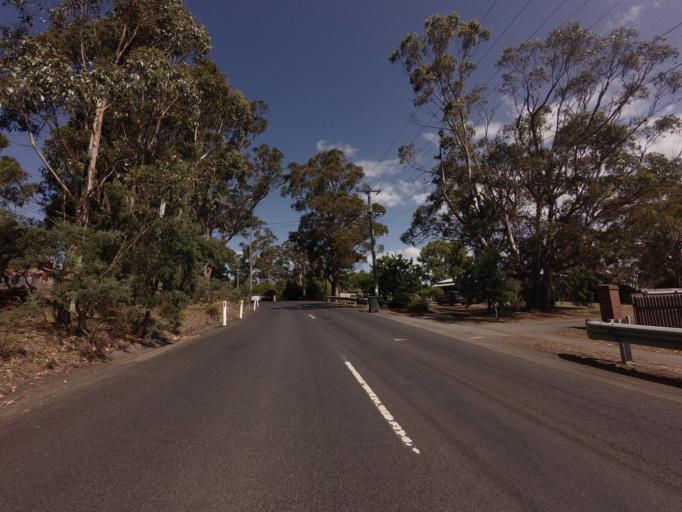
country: AU
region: Tasmania
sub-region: Hobart
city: Dynnyrne
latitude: -42.9227
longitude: 147.3242
